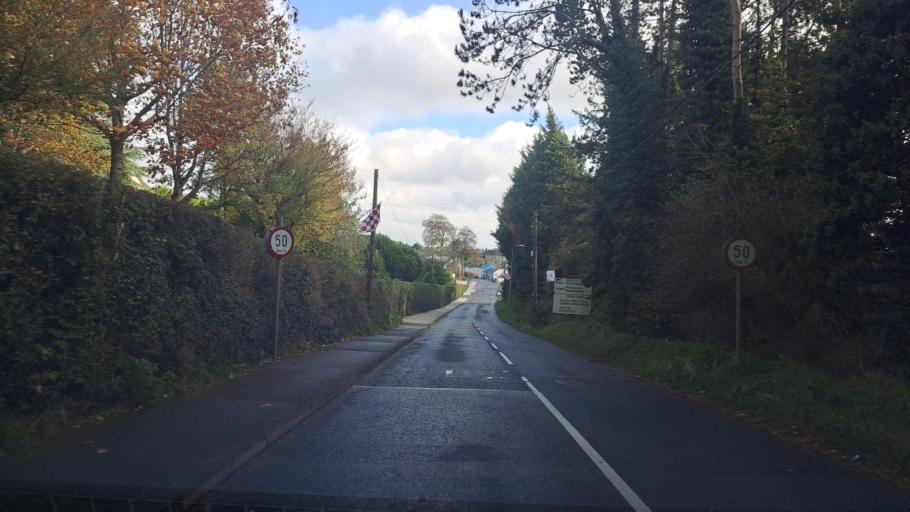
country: IE
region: Ulster
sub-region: County Monaghan
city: Monaghan
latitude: 54.1288
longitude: -6.9102
